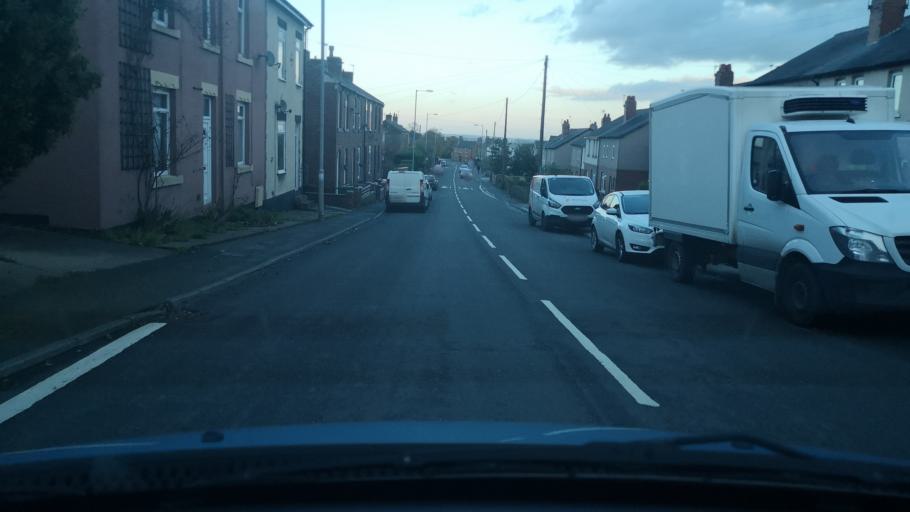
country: GB
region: England
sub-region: City and Borough of Wakefield
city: Middlestown
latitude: 53.6428
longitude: -1.5824
